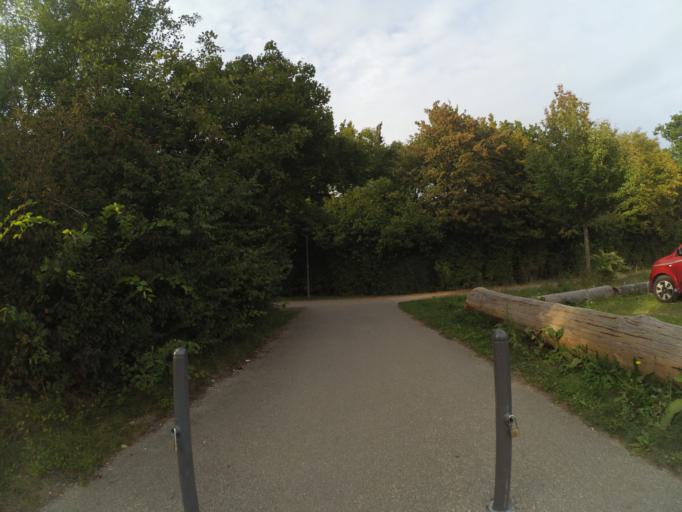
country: DE
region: Bavaria
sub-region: Upper Bavaria
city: Pasing
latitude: 48.1464
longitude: 11.5097
